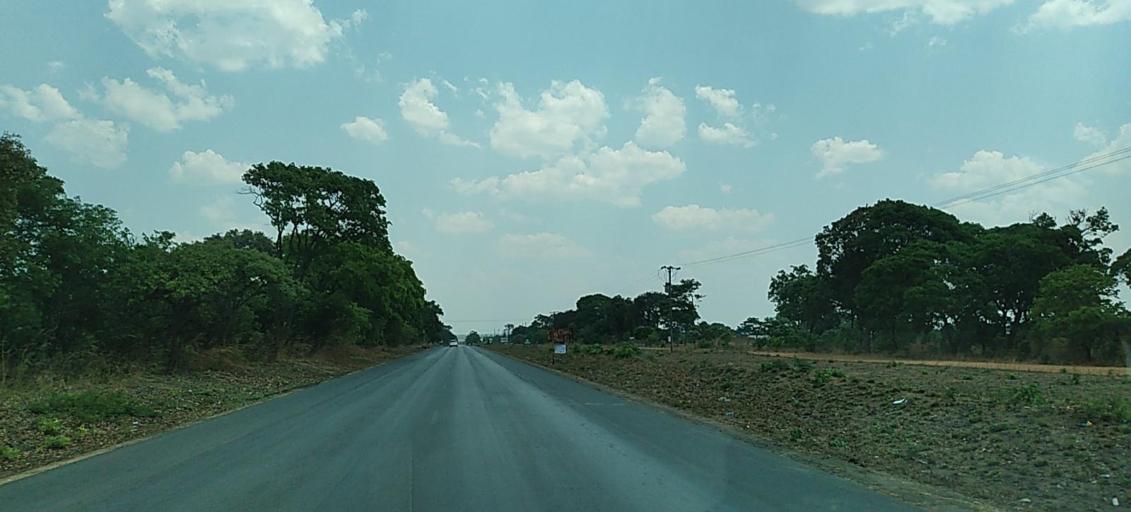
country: ZM
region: Central
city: Kabwe
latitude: -14.2782
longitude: 28.5530
